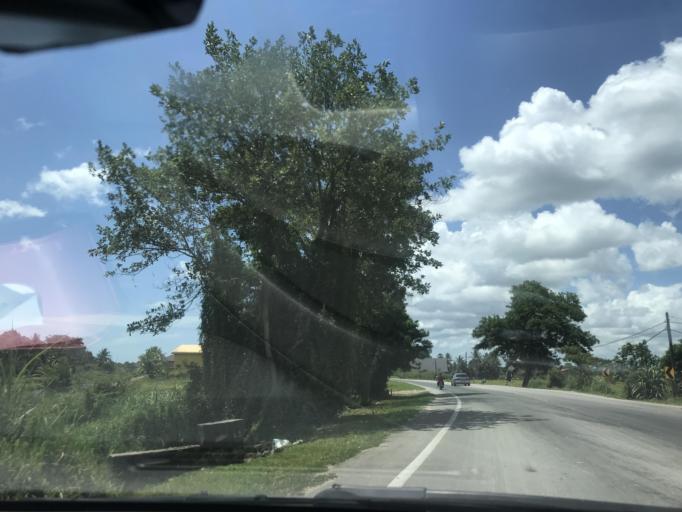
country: MY
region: Kelantan
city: Tumpat
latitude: 6.1952
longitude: 102.1373
